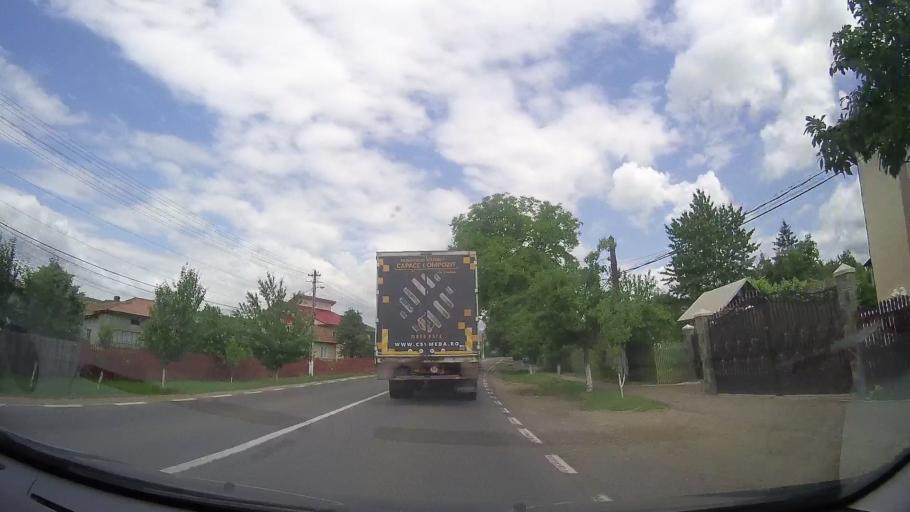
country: RO
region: Prahova
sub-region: Comuna Izvoarele
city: Homoraciu
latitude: 45.2573
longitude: 26.0192
